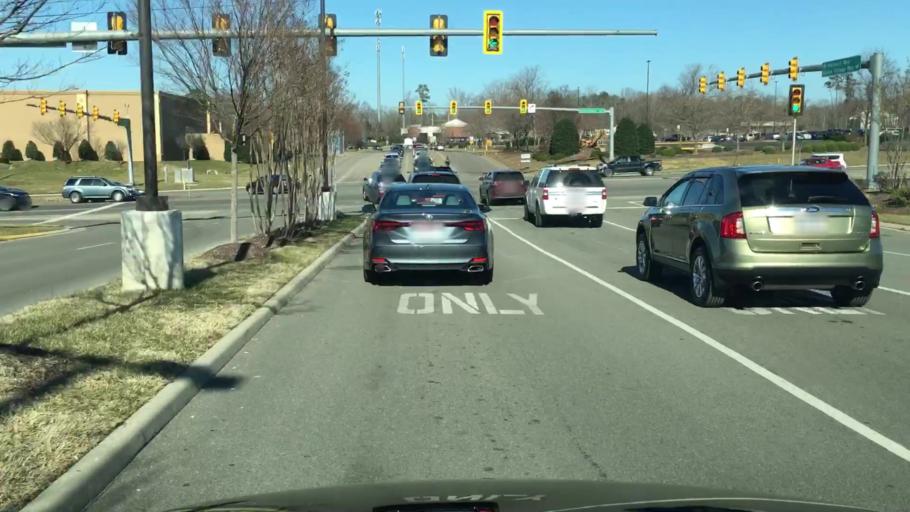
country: US
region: Virginia
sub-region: Chesterfield County
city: Bon Air
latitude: 37.5027
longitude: -77.6280
